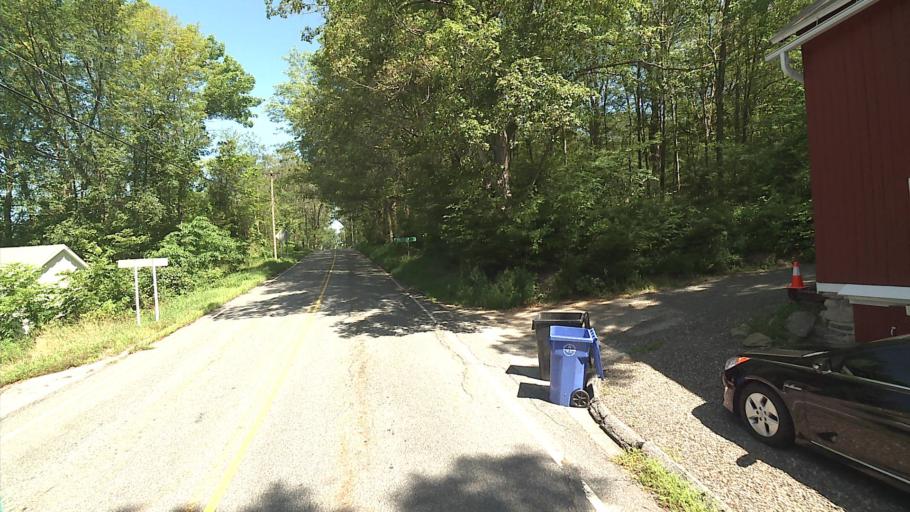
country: US
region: Connecticut
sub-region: Windham County
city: South Woodstock
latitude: 41.8616
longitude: -72.0065
